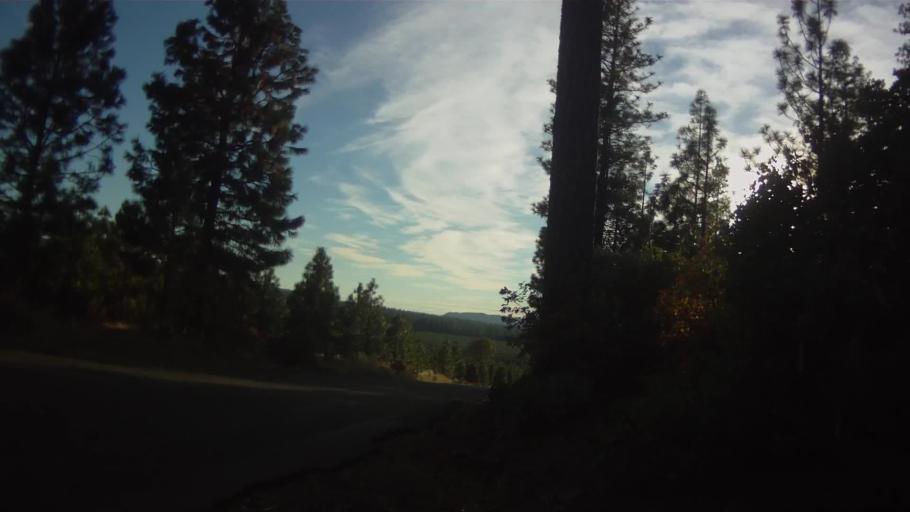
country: US
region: California
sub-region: Shasta County
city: Shingletown
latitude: 40.6349
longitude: -121.8513
